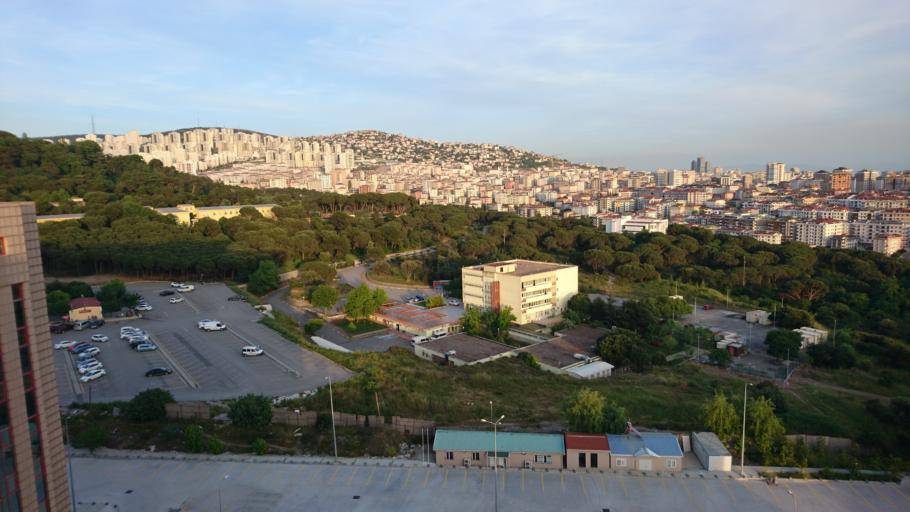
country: TR
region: Istanbul
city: Maltepe
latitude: 40.9501
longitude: 29.1378
